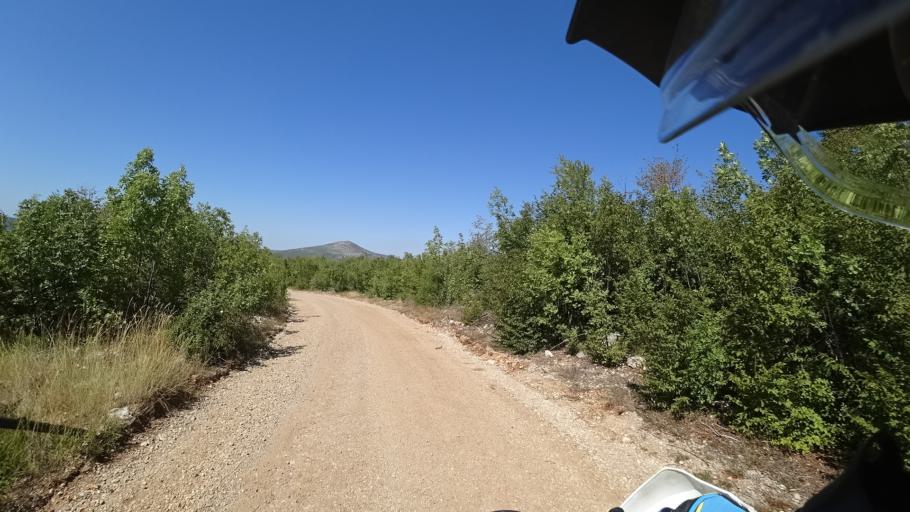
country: HR
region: Splitsko-Dalmatinska
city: Hrvace
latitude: 43.7543
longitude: 16.4491
